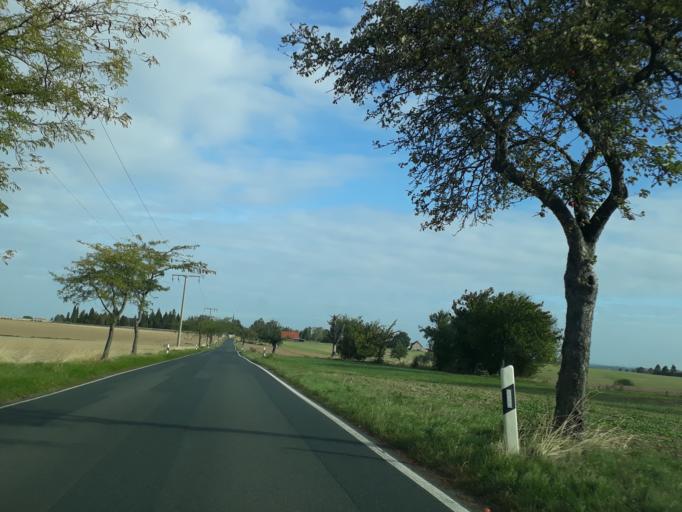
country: DE
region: Saxony
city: Klipphausen
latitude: 51.0786
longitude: 13.5796
